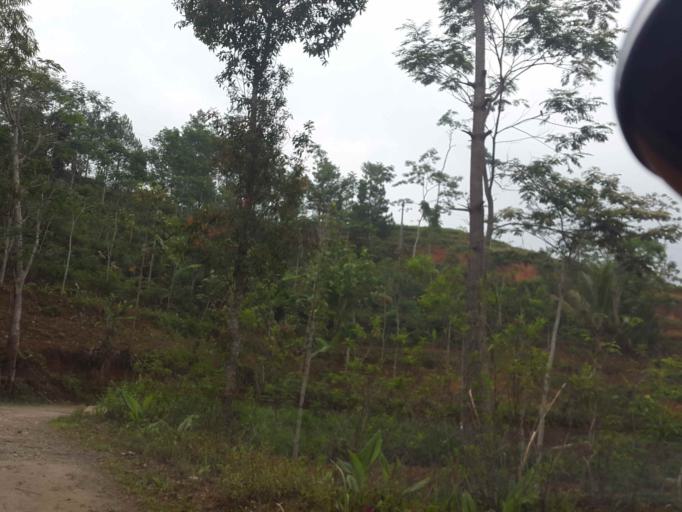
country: ID
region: East Java
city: Ploso
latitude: -8.0285
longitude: 111.1323
